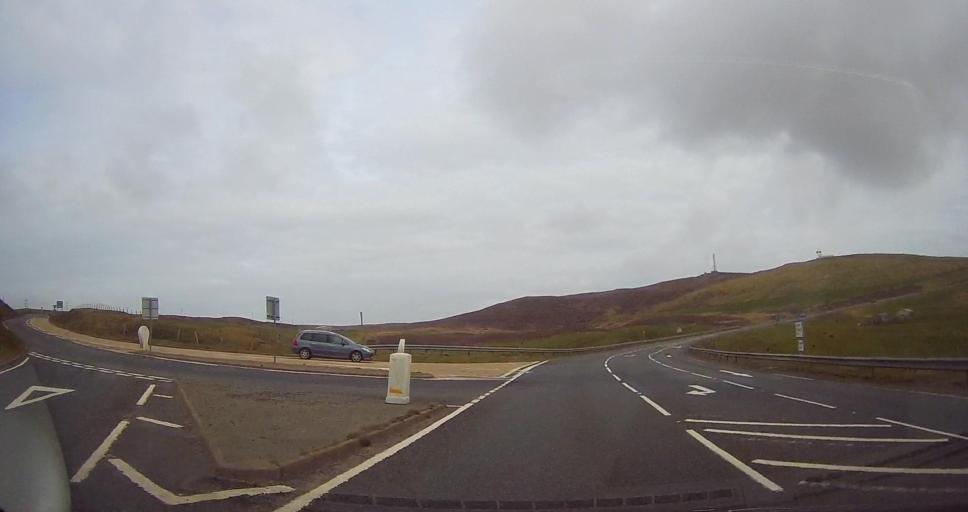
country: GB
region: Scotland
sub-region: Shetland Islands
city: Lerwick
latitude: 60.1360
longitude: -1.2138
